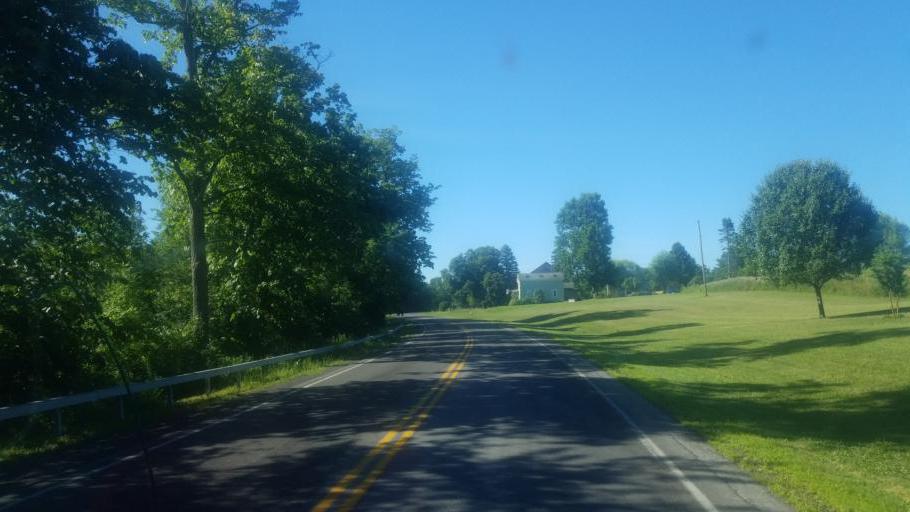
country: US
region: New York
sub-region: Ontario County
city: Clifton Springs
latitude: 42.8481
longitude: -77.1088
